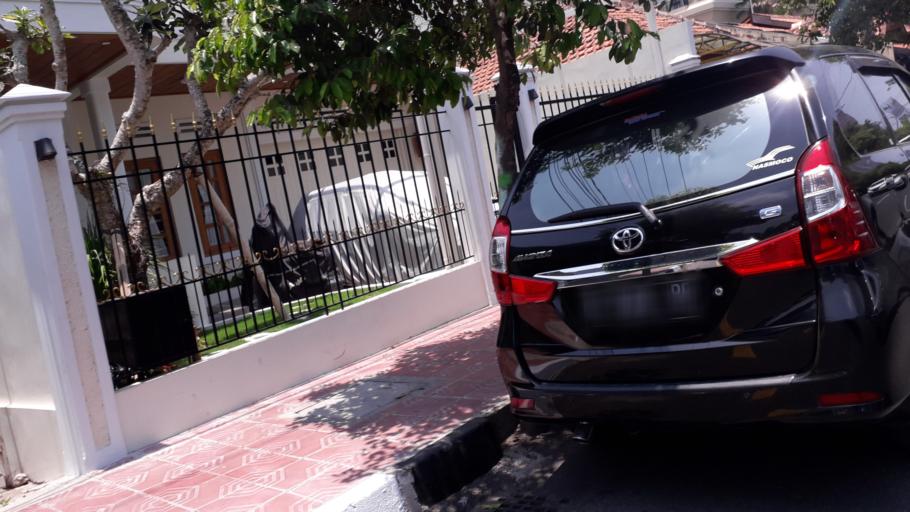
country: ID
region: Daerah Istimewa Yogyakarta
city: Yogyakarta
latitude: -7.7727
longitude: 110.3682
